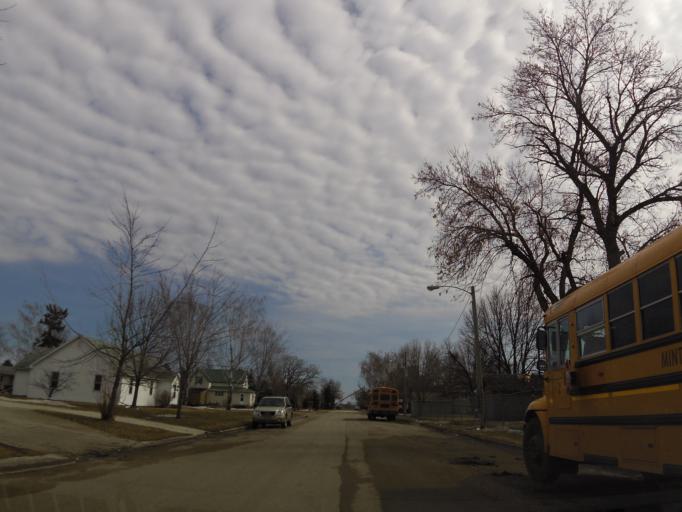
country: US
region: North Dakota
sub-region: Walsh County
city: Grafton
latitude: 48.2936
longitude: -97.3741
